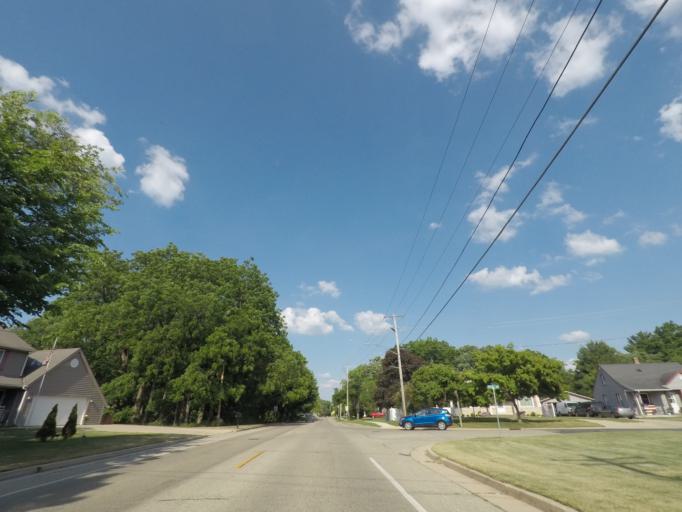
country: US
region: Wisconsin
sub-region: Walworth County
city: East Troy
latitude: 42.7917
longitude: -88.4101
